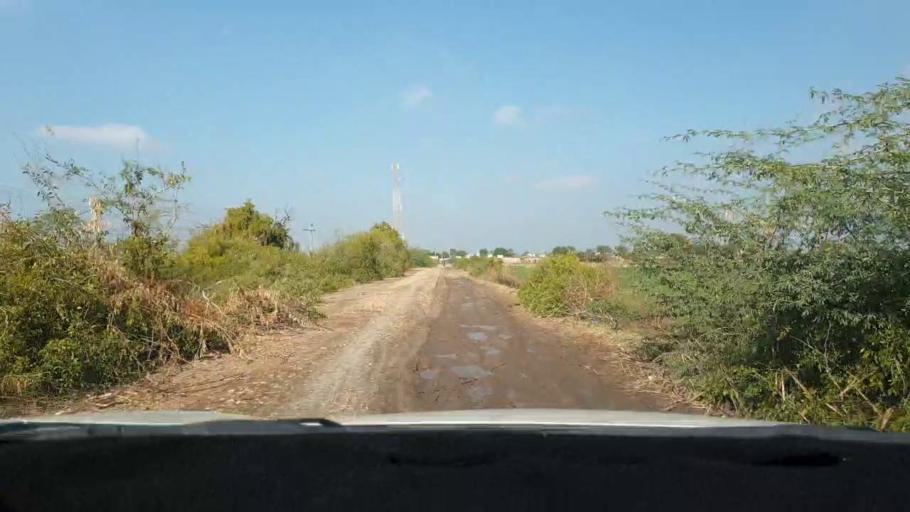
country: PK
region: Sindh
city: Berani
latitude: 25.7743
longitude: 68.8605
